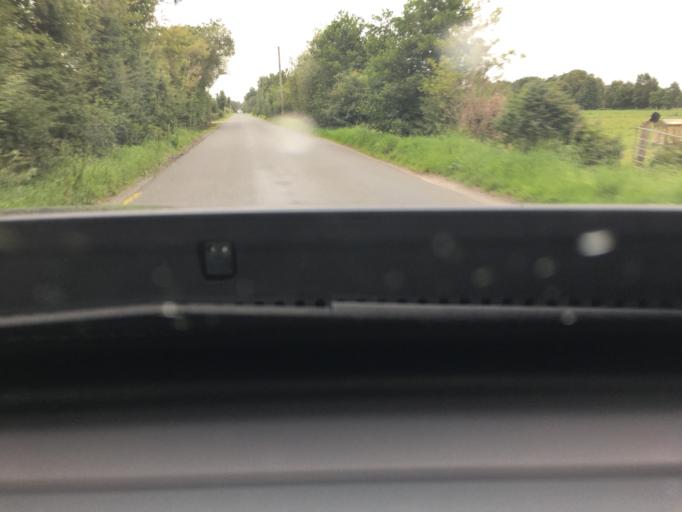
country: GB
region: Northern Ireland
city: Moy
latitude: 54.5072
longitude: -6.6374
